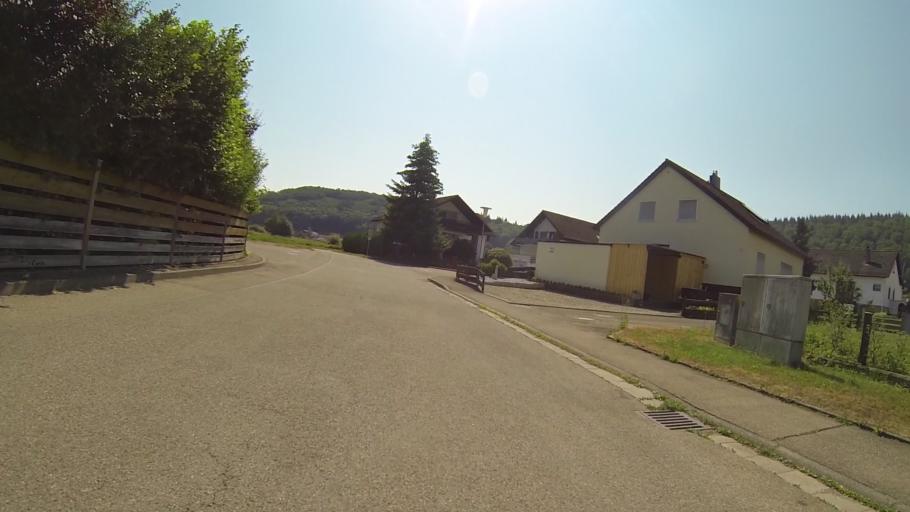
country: DE
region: Baden-Wuerttemberg
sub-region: Regierungsbezirk Stuttgart
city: Konigsbronn
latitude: 48.7309
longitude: 10.1410
